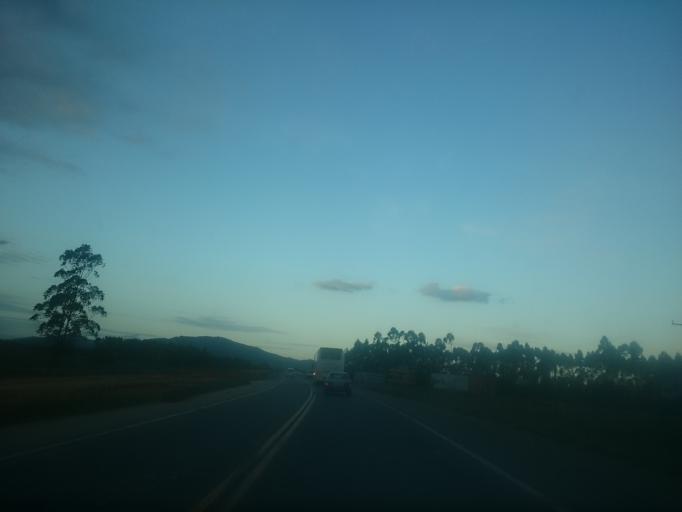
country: BR
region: Santa Catarina
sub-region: Gaspar
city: Gaspar
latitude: -26.8785
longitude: -48.8293
